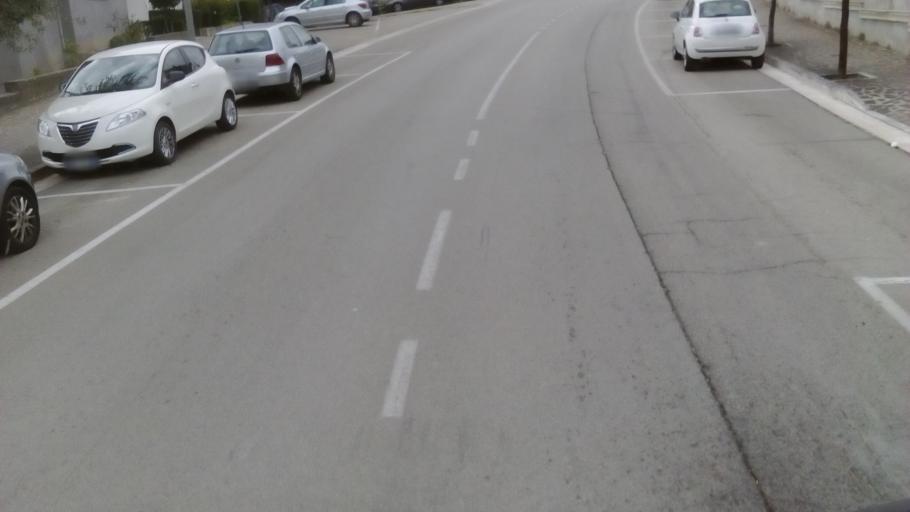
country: IT
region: Abruzzo
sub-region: Provincia di Chieti
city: San Salvo
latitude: 42.0513
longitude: 14.7321
